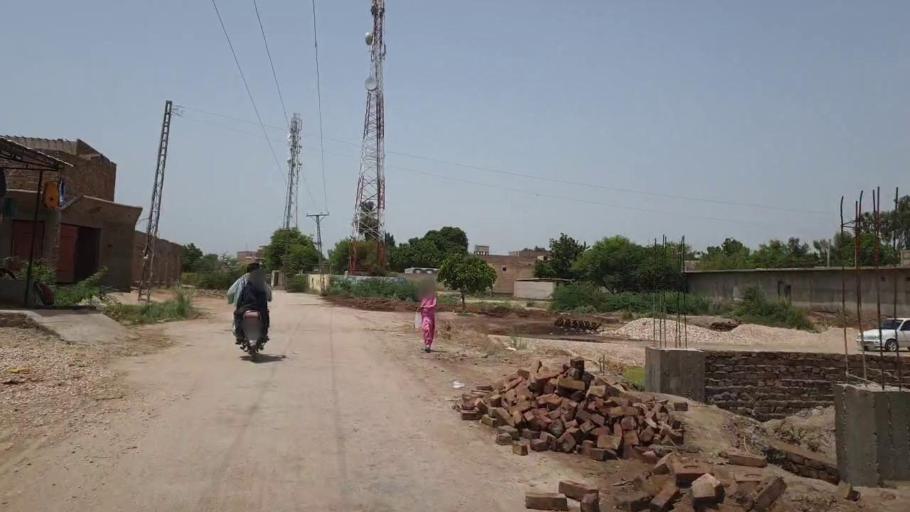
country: PK
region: Sindh
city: Daur
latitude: 26.3984
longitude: 68.4387
